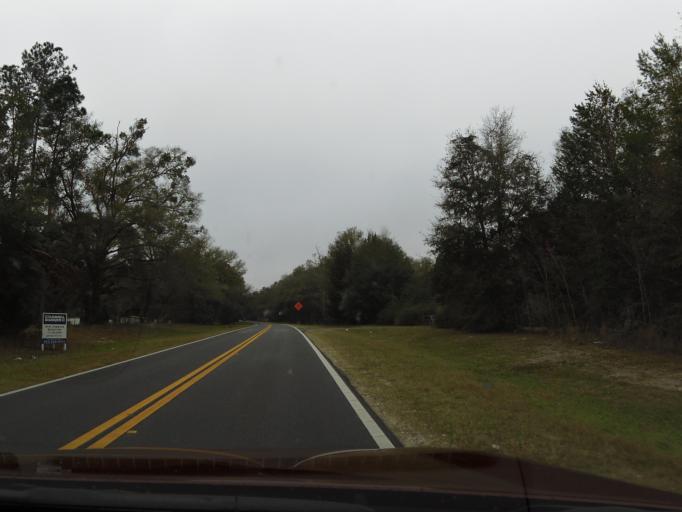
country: US
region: Florida
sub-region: Alachua County
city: High Springs
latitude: 29.8503
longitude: -82.5814
